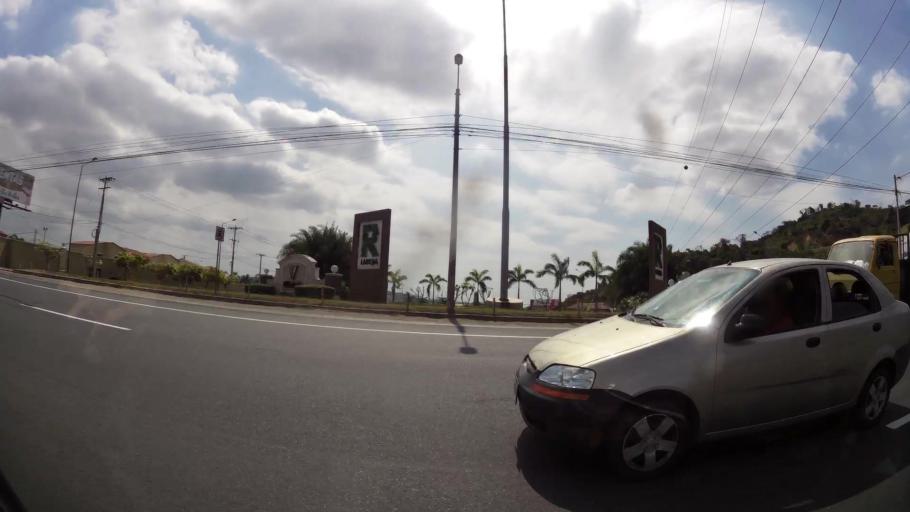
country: EC
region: Guayas
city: El Triunfo
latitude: -2.0592
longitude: -79.9256
